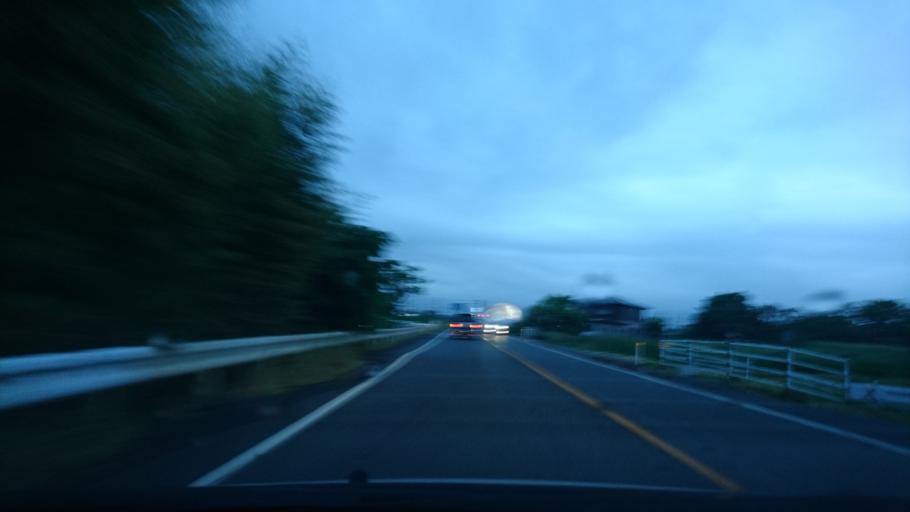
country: JP
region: Iwate
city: Ichinoseki
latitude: 38.8132
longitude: 141.0774
